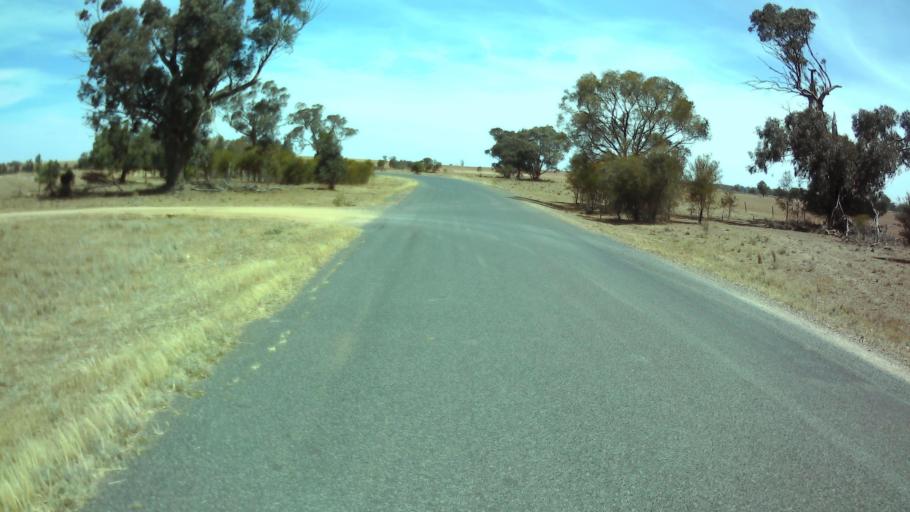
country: AU
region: New South Wales
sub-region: Weddin
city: Grenfell
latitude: -33.8862
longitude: 147.7419
